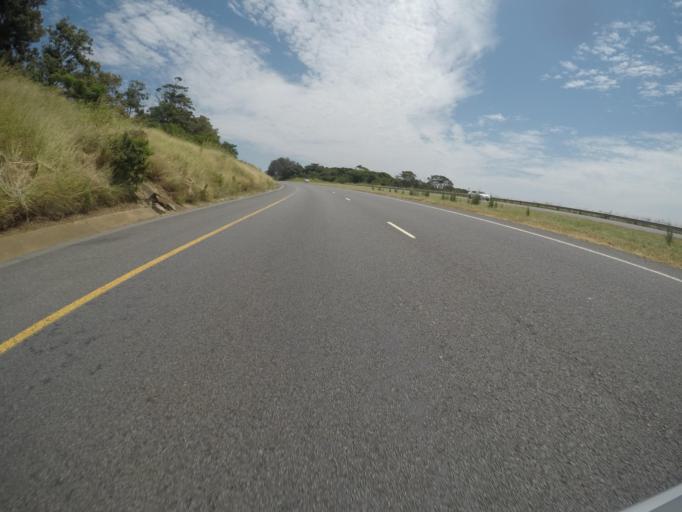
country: ZA
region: Eastern Cape
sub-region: Buffalo City Metropolitan Municipality
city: East London
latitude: -32.9680
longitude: 27.8780
